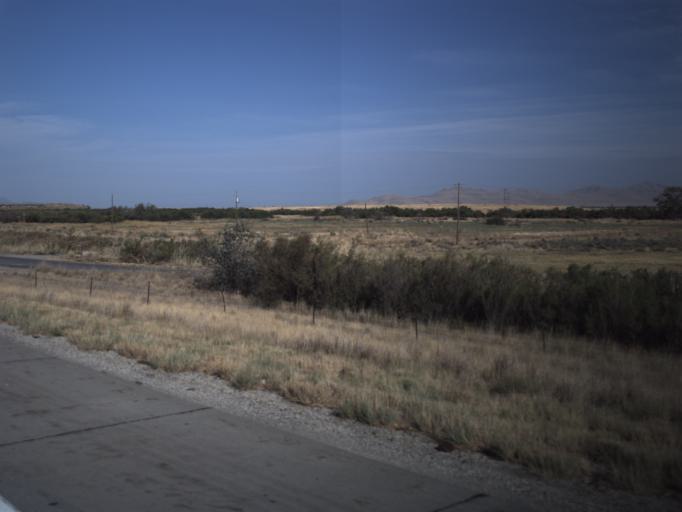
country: US
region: Utah
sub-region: Salt Lake County
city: Magna
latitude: 40.7712
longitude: -112.0447
